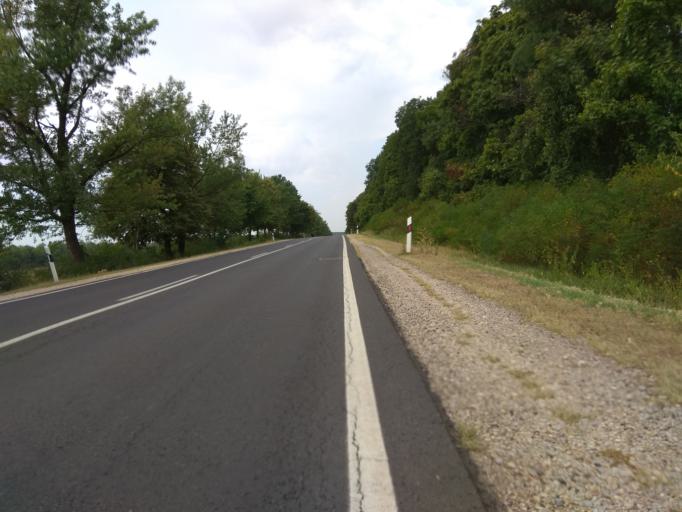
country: HU
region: Borsod-Abauj-Zemplen
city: Harsany
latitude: 47.9235
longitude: 20.7559
